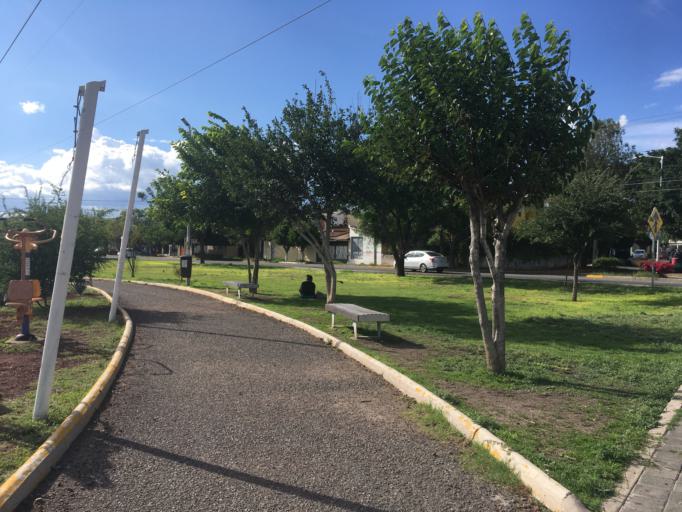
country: MX
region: Queretaro
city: San Jose el Alto
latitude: 20.6217
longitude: -100.3918
